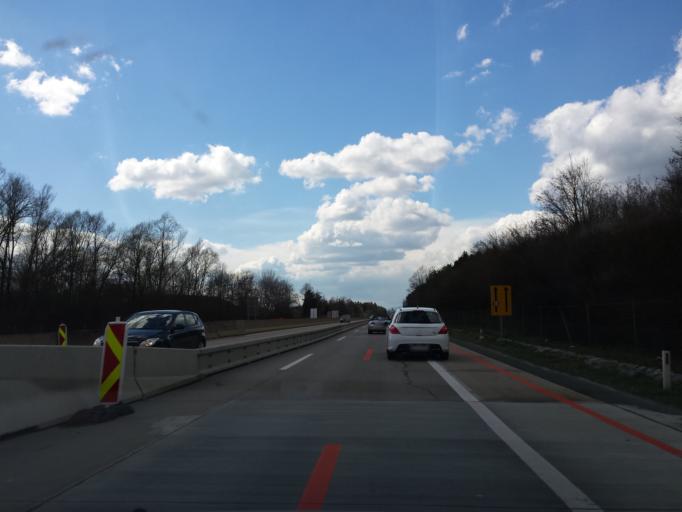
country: AT
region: Styria
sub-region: Politischer Bezirk Graz-Umgebung
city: Unterpremstatten
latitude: 46.9721
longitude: 15.3893
